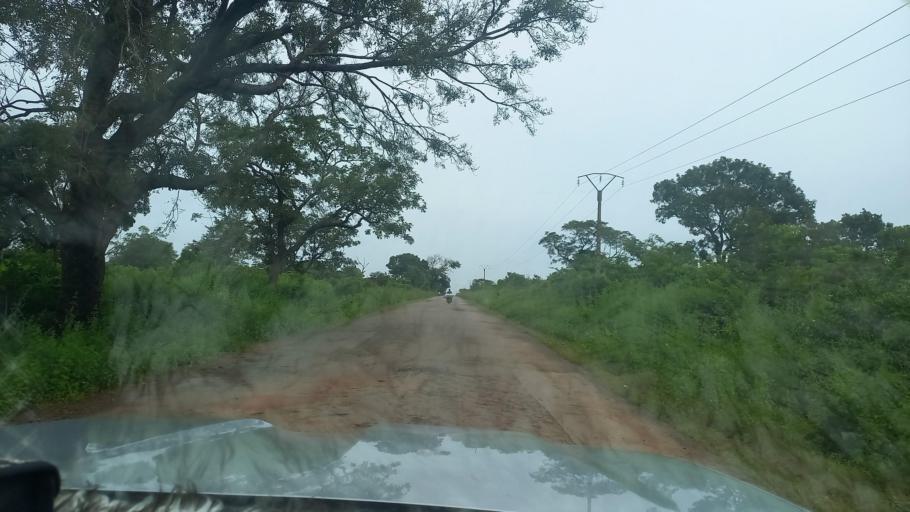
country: SN
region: Ziguinchor
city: Bignona
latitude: 12.8284
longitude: -16.1683
